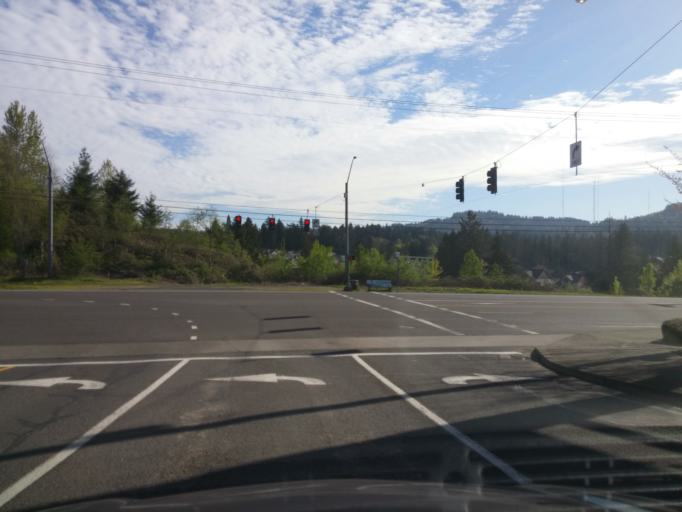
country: US
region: Oregon
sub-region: Washington County
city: Cedar Hills
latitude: 45.5153
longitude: -122.7902
